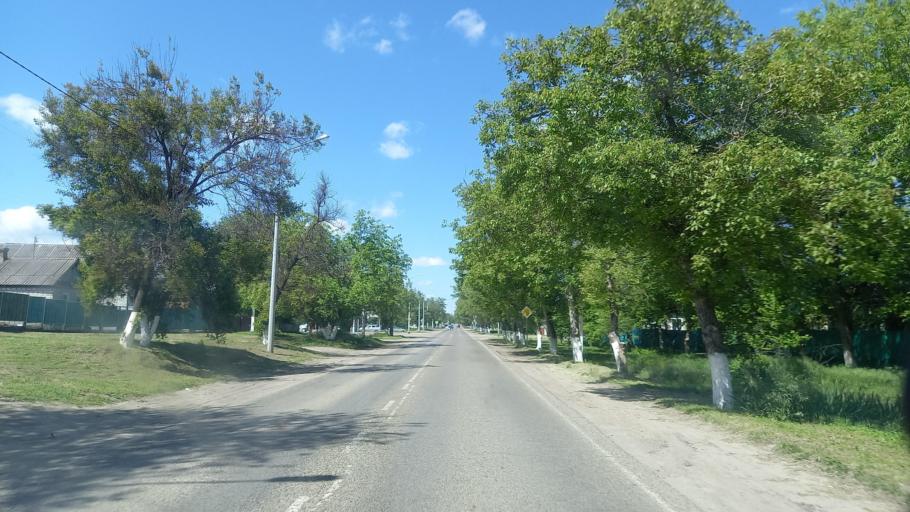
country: RU
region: Krasnodarskiy
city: Novoukrainskoye
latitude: 45.3804
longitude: 40.5182
